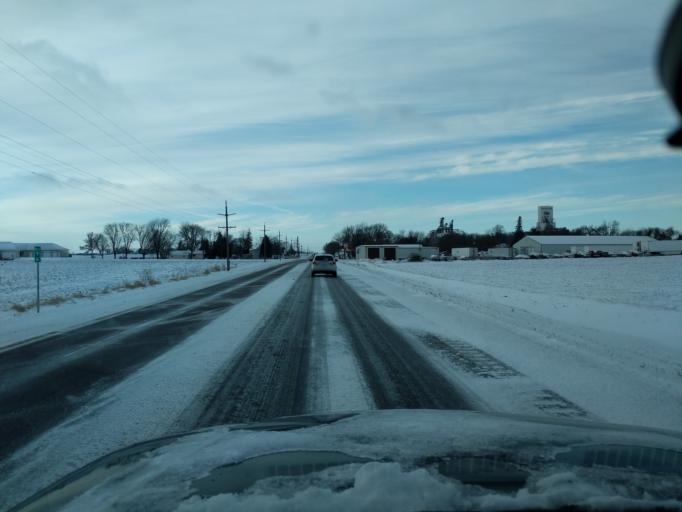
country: US
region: Minnesota
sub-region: Renville County
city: Hector
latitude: 44.7320
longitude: -94.6135
